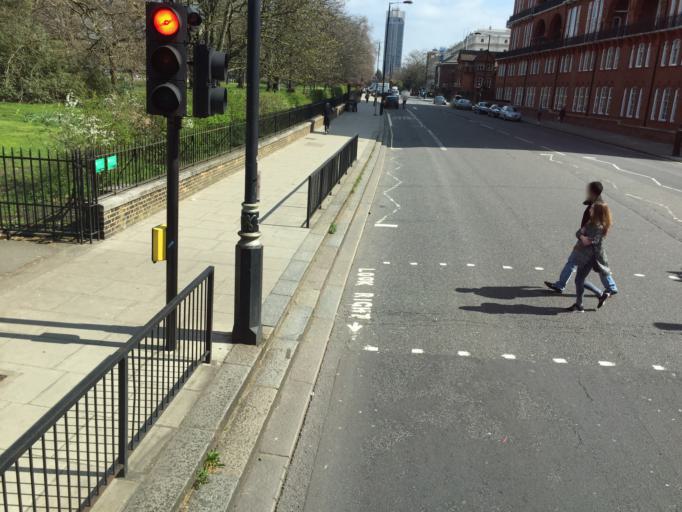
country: GB
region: England
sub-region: Greater London
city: Bayswater
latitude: 51.5016
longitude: -0.1773
